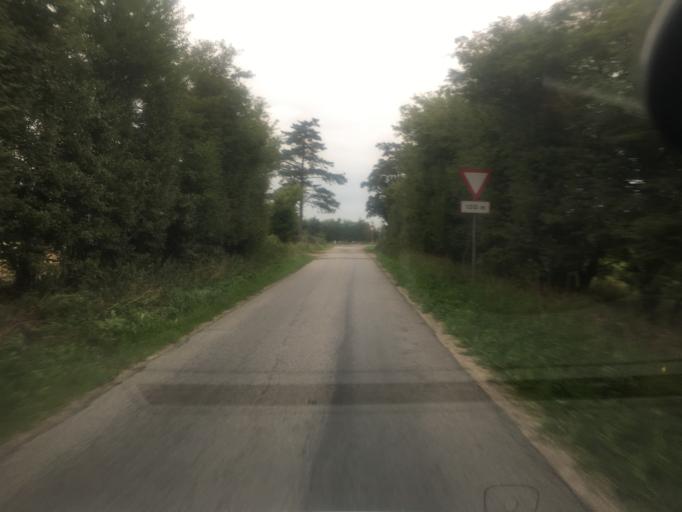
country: DK
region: South Denmark
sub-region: Tonder Kommune
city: Logumkloster
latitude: 55.0410
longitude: 9.0081
